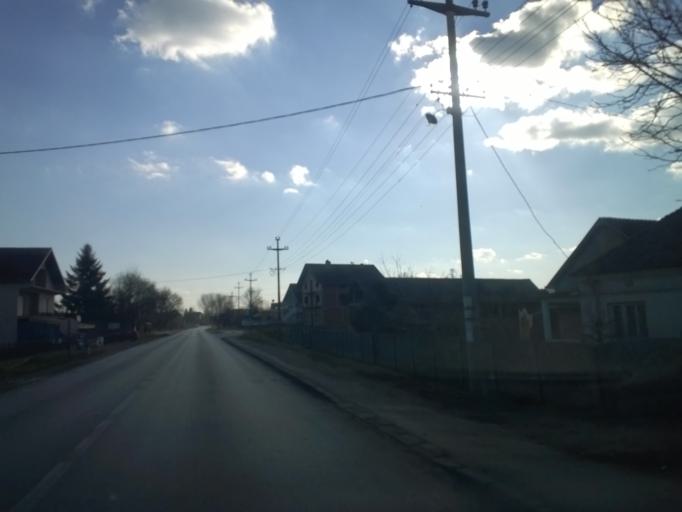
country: RS
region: Central Serbia
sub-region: Podunavski Okrug
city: Smederevo
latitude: 44.5920
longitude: 20.9708
